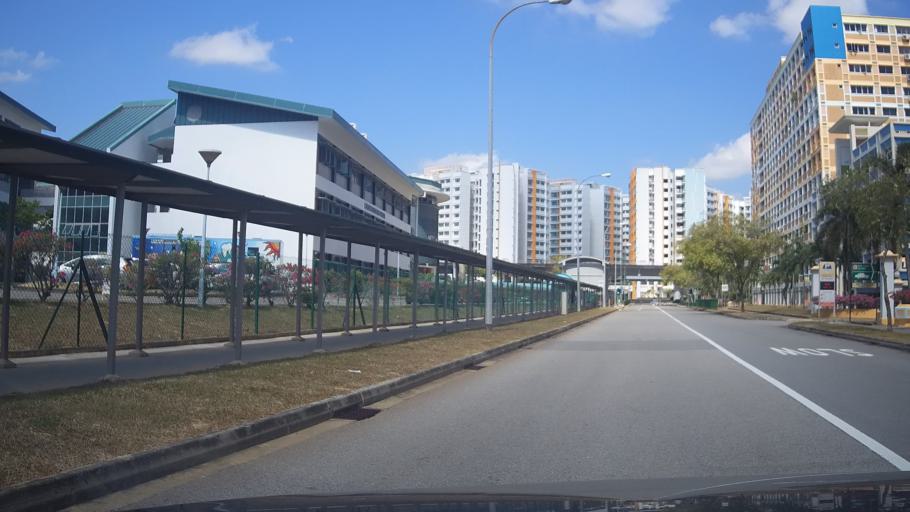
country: MY
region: Johor
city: Kampung Pasir Gudang Baru
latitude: 1.3681
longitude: 103.9500
